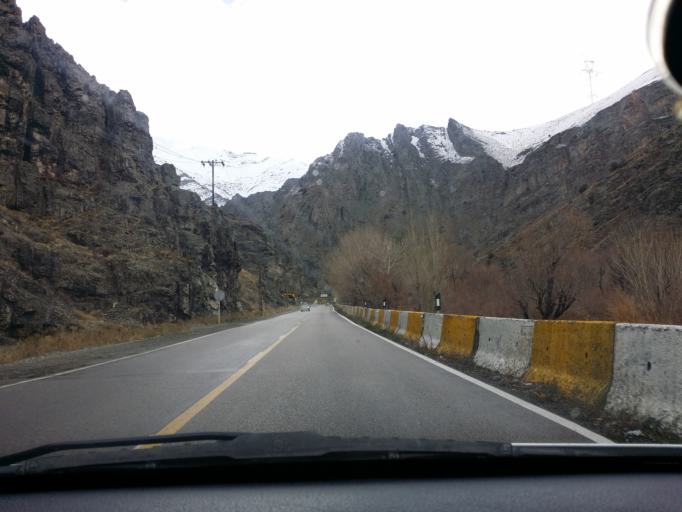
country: IR
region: Tehran
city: Tajrish
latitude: 36.0145
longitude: 51.2868
